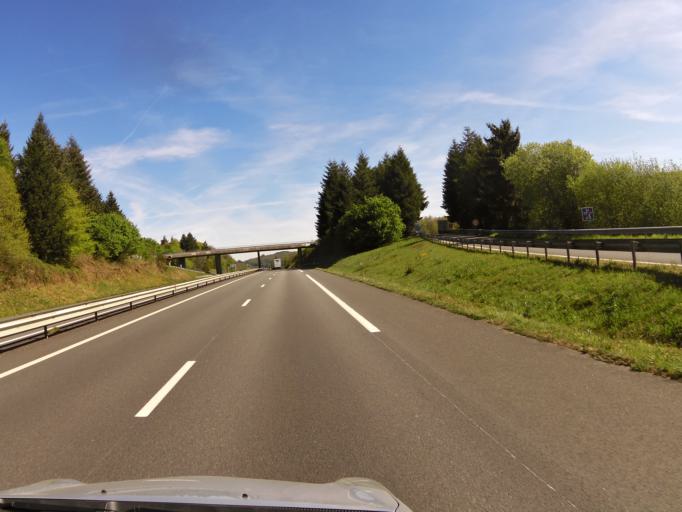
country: FR
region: Limousin
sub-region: Departement de la Haute-Vienne
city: Razes
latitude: 46.0243
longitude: 1.3448
